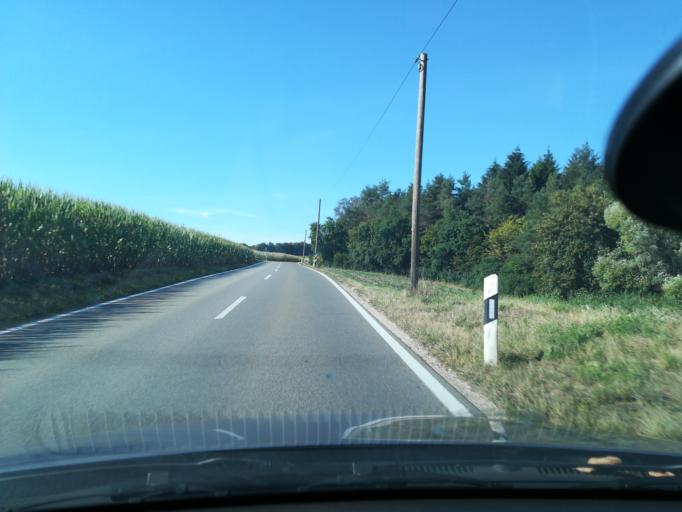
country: DE
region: Baden-Wuerttemberg
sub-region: Freiburg Region
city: Moos
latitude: 47.7423
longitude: 8.8979
